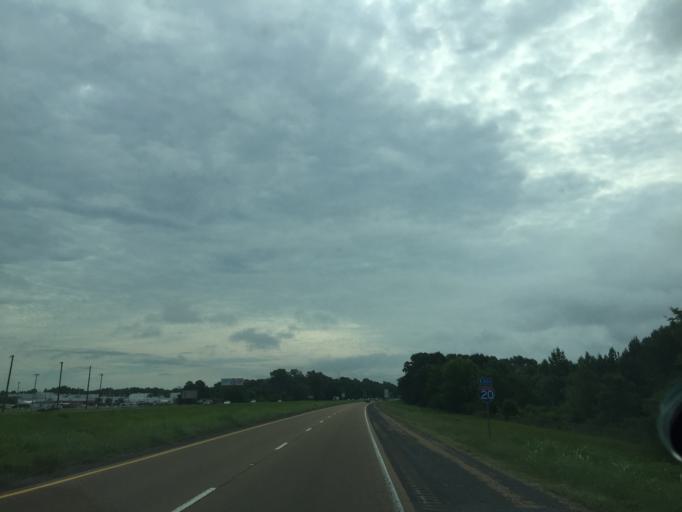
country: US
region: Mississippi
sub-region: Rankin County
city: Brandon
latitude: 32.2795
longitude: -90.0266
